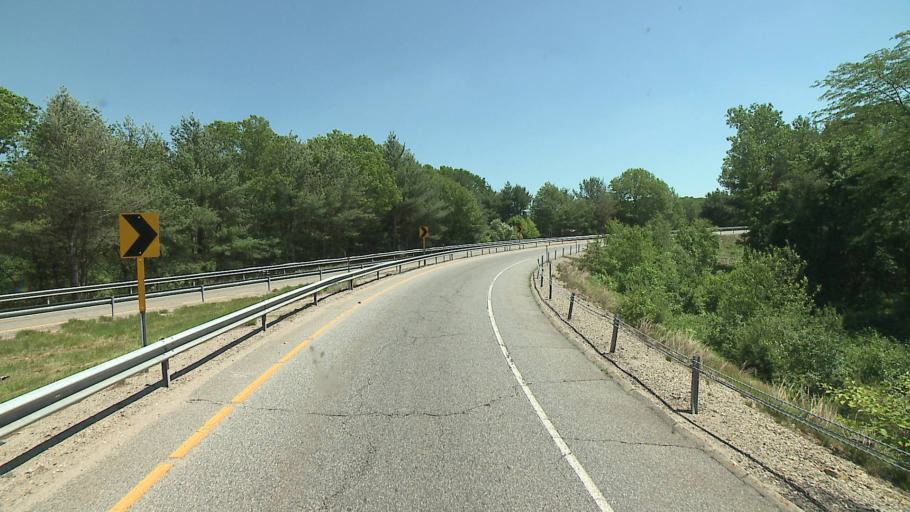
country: US
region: Connecticut
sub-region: Windham County
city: Putnam
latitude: 41.9003
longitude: -71.8971
